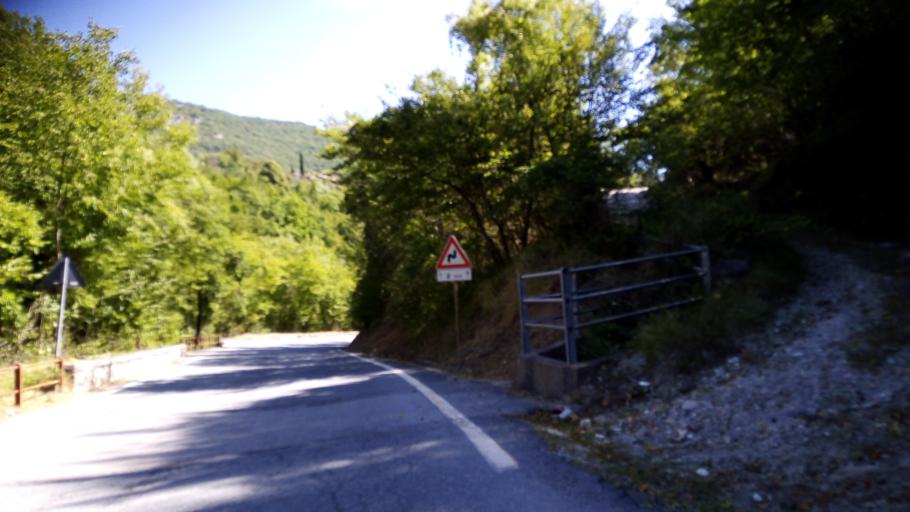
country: IT
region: Liguria
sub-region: Provincia di Savona
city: Balestrino
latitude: 44.1386
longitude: 8.1595
